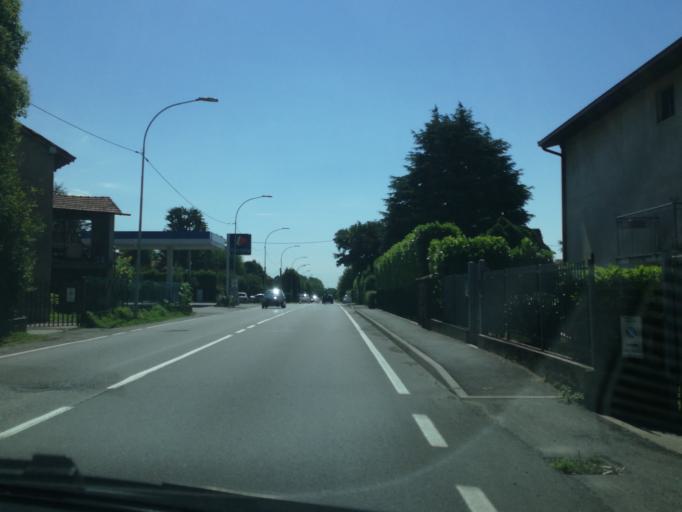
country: IT
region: Lombardy
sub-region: Provincia di Bergamo
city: Piazza Caduti
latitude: 45.6990
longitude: 9.4968
